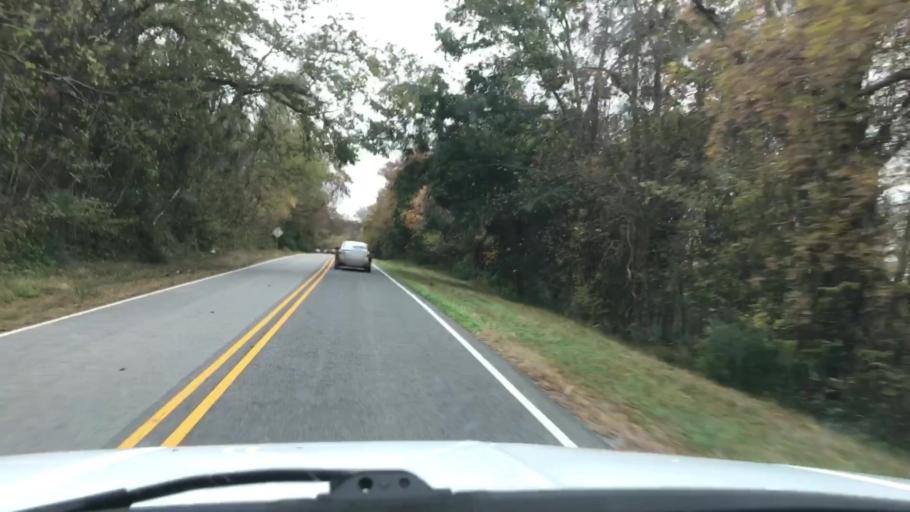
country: US
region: Virginia
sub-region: Goochland County
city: Goochland
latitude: 37.6222
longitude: -77.7755
